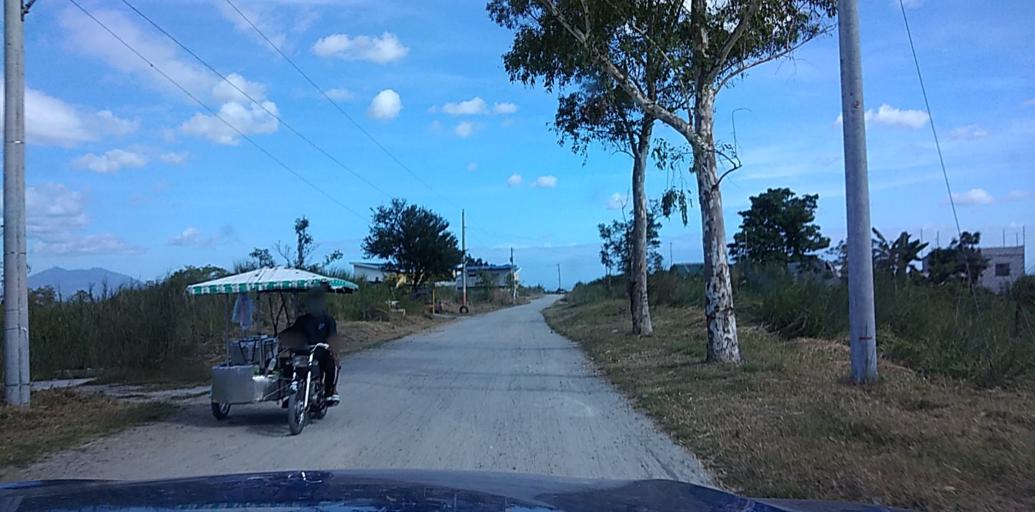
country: PH
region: Central Luzon
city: Santol
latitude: 15.1432
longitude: 120.5257
